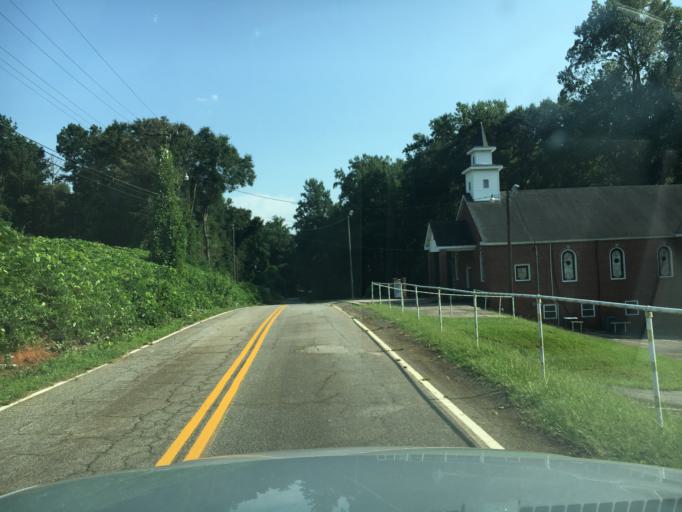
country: US
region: South Carolina
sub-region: Spartanburg County
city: Duncan
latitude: 34.9350
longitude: -82.1422
